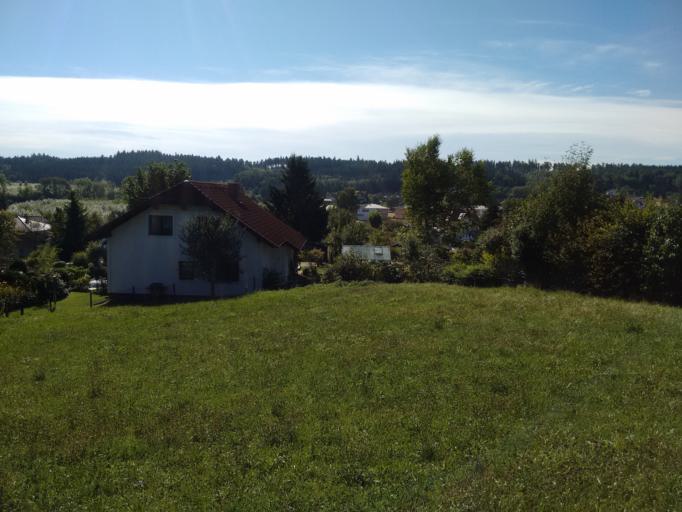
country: AT
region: Upper Austria
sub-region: Wels-Land
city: Buchkirchen
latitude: 48.1956
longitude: 13.9705
